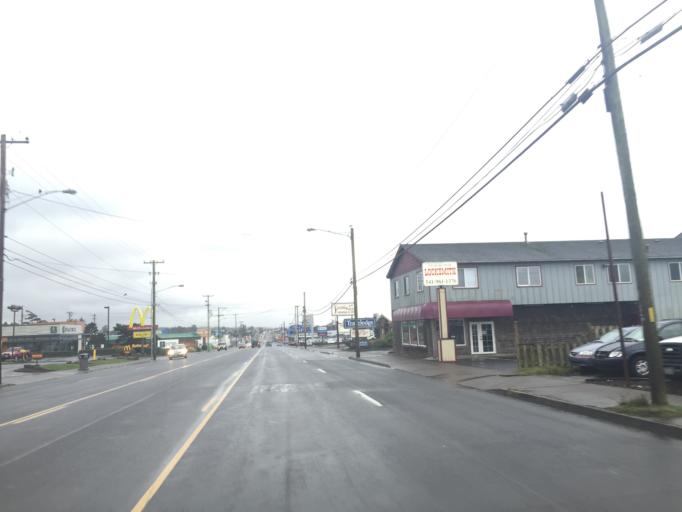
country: US
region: Oregon
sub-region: Lincoln County
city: Newport
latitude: 44.6473
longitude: -124.0531
